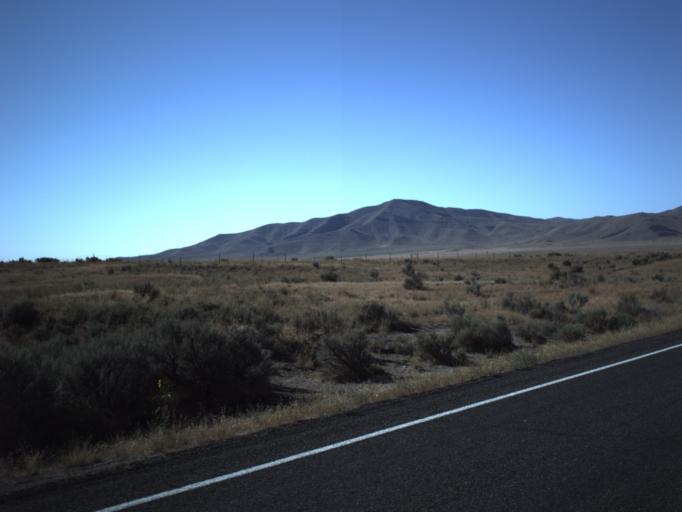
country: US
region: Utah
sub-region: Juab County
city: Mona
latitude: 39.7188
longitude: -112.1999
